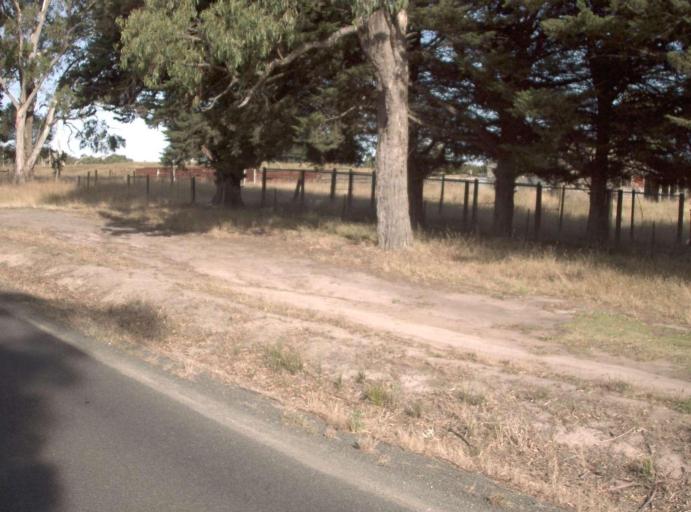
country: AU
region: Victoria
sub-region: Latrobe
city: Morwell
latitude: -38.2692
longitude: 146.4726
